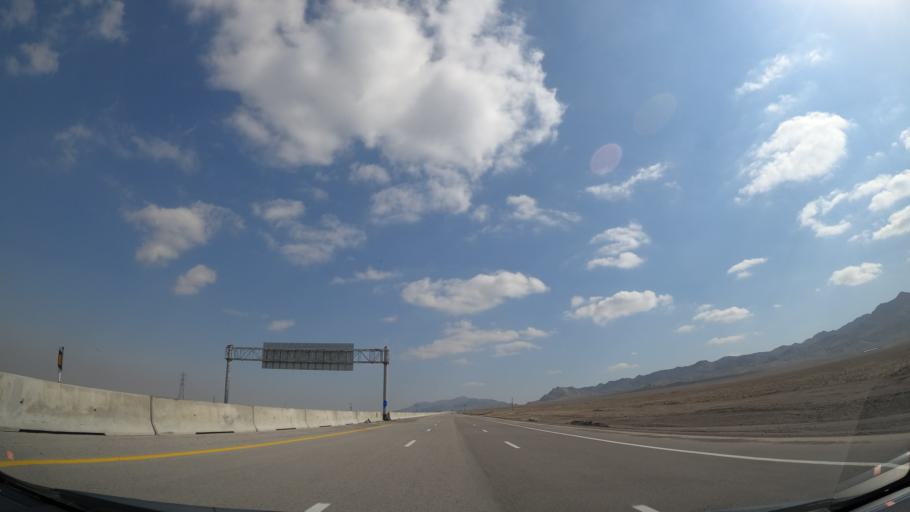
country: IR
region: Alborz
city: Eshtehard
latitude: 35.7154
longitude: 50.5813
